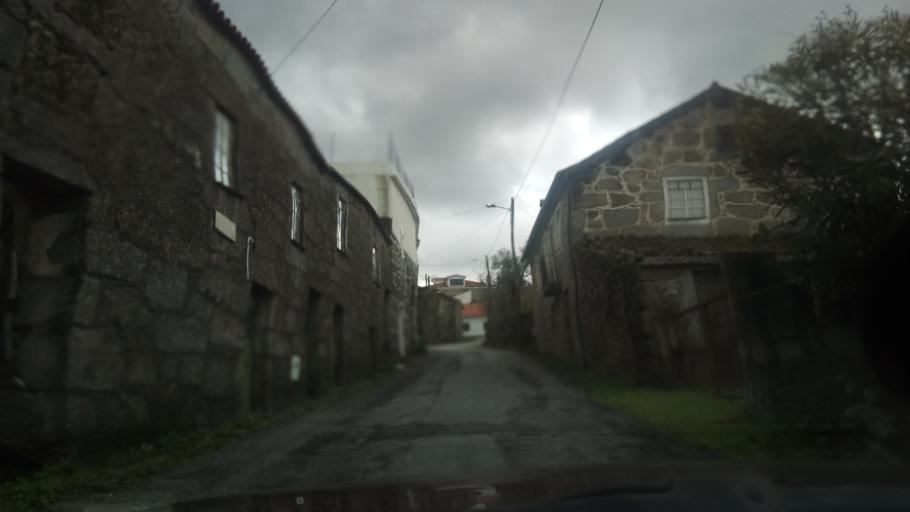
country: PT
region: Guarda
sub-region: Celorico da Beira
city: Celorico da Beira
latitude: 40.5578
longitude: -7.4570
